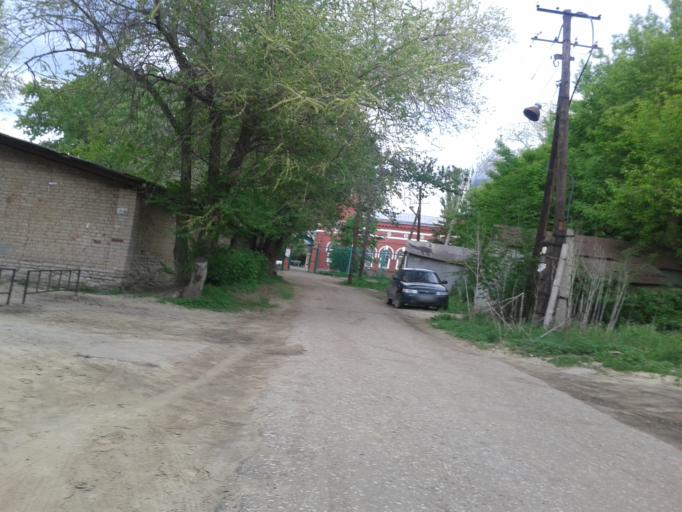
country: RU
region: Volgograd
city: Krasnoslobodsk
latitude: 48.5213
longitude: 44.5112
